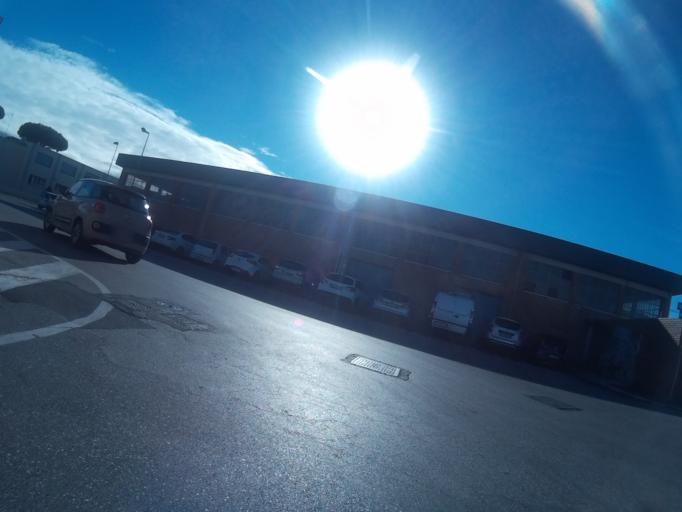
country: IT
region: Tuscany
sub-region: Provincia di Livorno
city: Livorno
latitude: 43.5669
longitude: 10.3356
